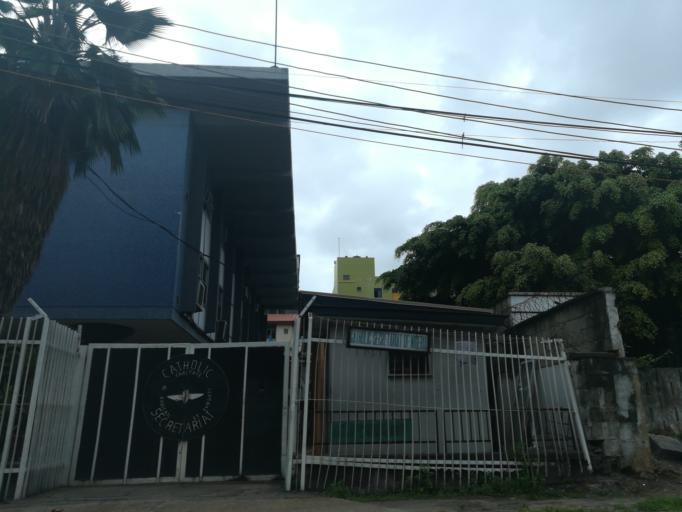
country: NG
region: Lagos
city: Lagos
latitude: 6.4450
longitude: 3.4013
